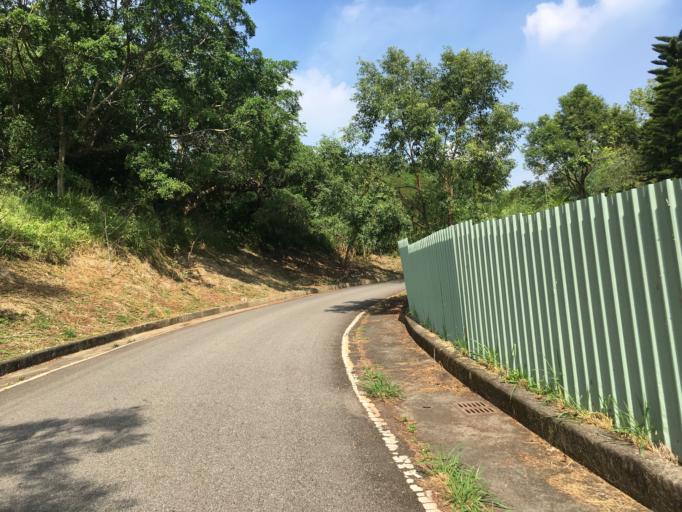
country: TW
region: Taiwan
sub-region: Taichung City
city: Taichung
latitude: 24.1774
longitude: 120.7567
